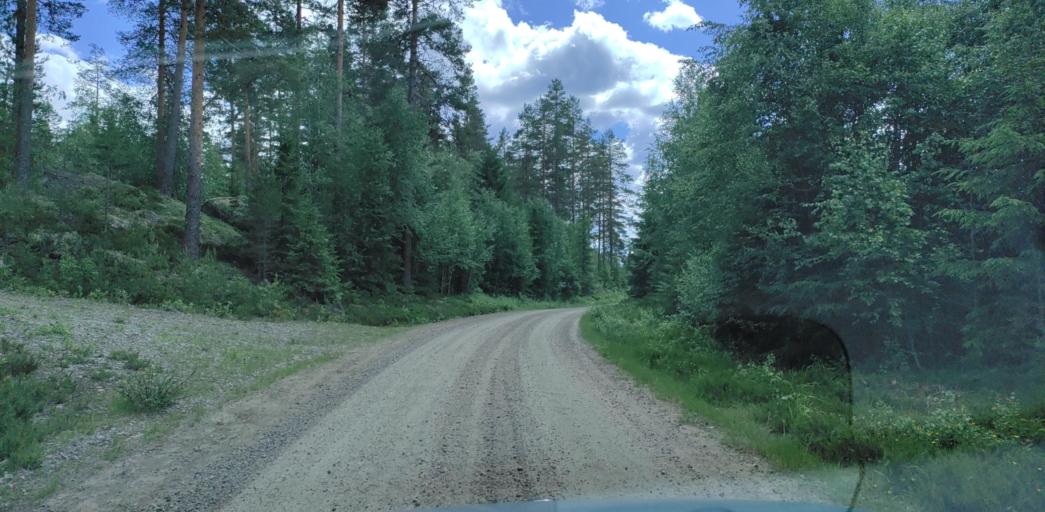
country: SE
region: Vaermland
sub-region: Hagfors Kommun
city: Ekshaerad
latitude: 60.0691
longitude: 13.2907
